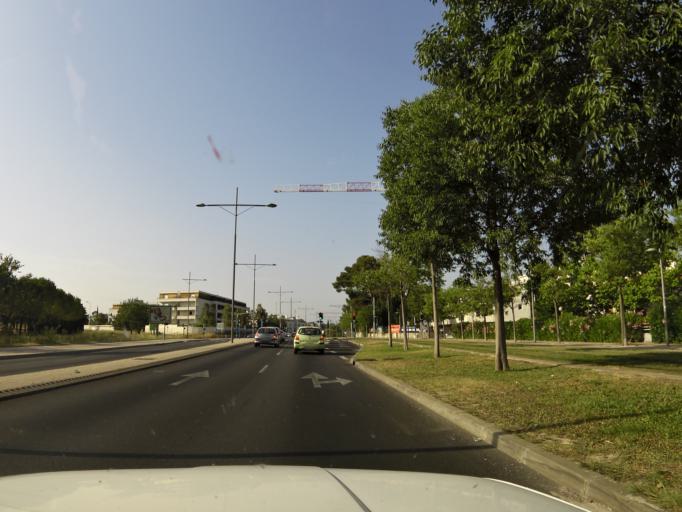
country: FR
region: Languedoc-Roussillon
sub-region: Departement de l'Herault
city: Montferrier-sur-Lez
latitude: 43.6329
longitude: 3.8431
